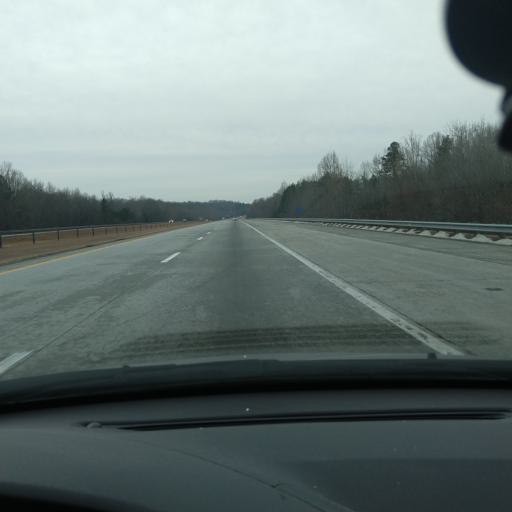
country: US
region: North Carolina
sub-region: Davidson County
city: Lexington
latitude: 35.8614
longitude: -80.2701
